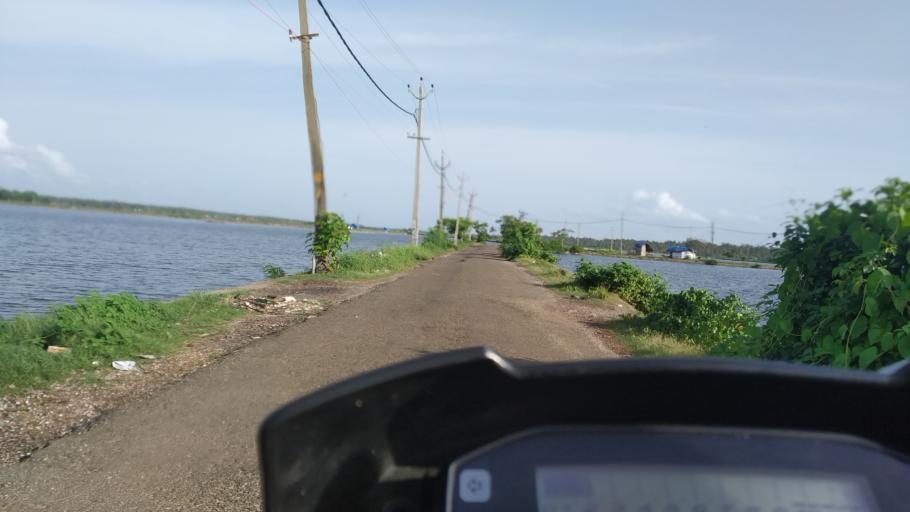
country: IN
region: Kerala
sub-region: Thrissur District
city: Kodungallur
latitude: 10.1294
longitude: 76.1874
